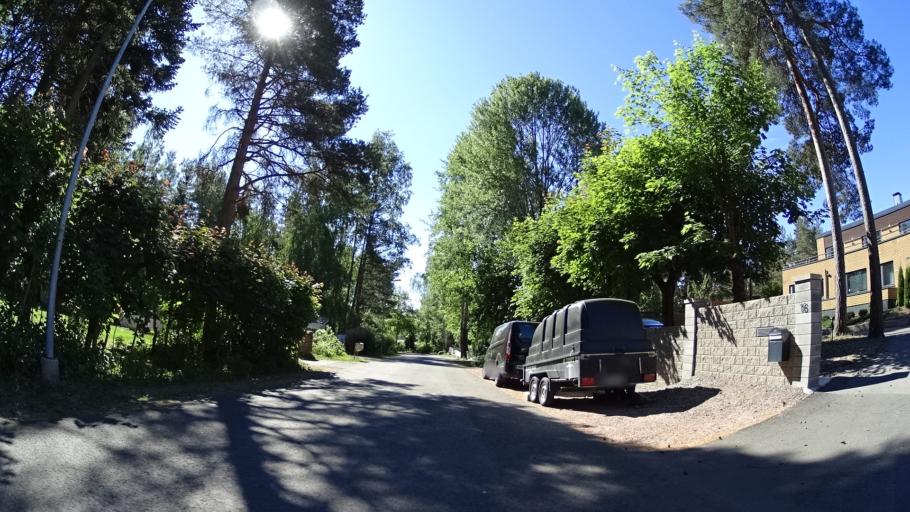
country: FI
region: Uusimaa
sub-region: Helsinki
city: Kauniainen
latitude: 60.2135
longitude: 24.7102
